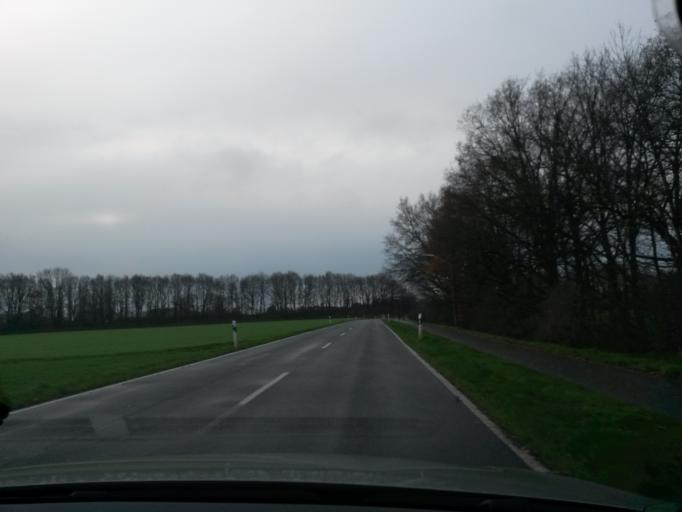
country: DE
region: North Rhine-Westphalia
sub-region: Regierungsbezirk Dusseldorf
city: Alpen
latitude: 51.5991
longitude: 6.5022
